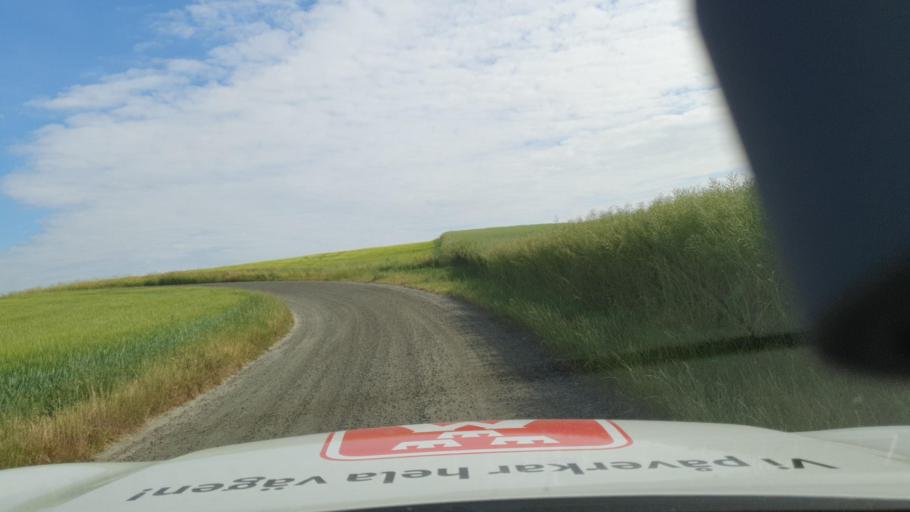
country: SE
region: Skane
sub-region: Skurups Kommun
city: Skivarp
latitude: 55.4339
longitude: 13.5953
